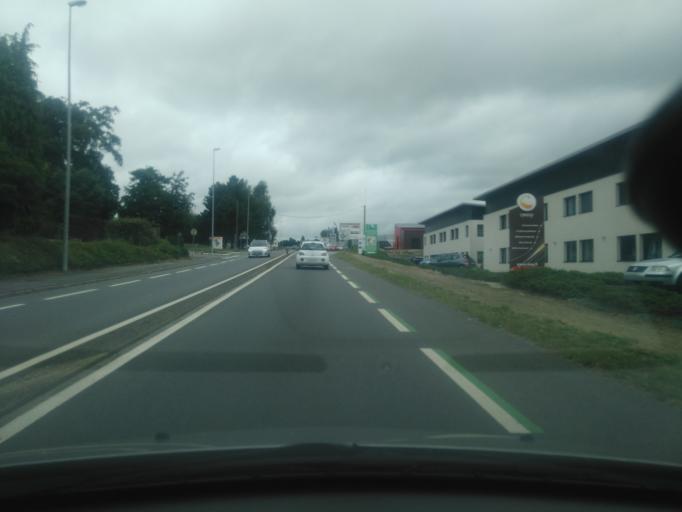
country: FR
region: Brittany
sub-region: Departement des Cotes-d'Armor
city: Lehon
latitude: 48.4618
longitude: -2.0581
